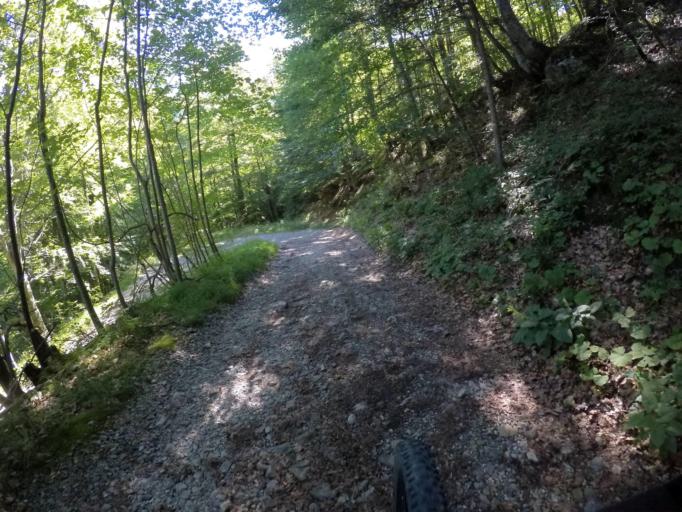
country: IT
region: Friuli Venezia Giulia
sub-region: Provincia di Udine
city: Paularo
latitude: 46.4672
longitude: 13.1064
